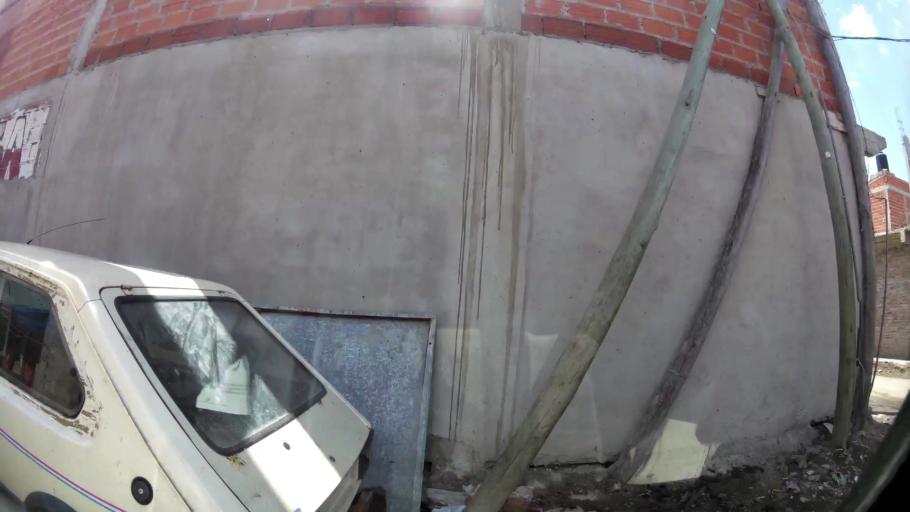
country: AR
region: Buenos Aires F.D.
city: Villa Lugano
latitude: -34.6886
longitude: -58.4435
